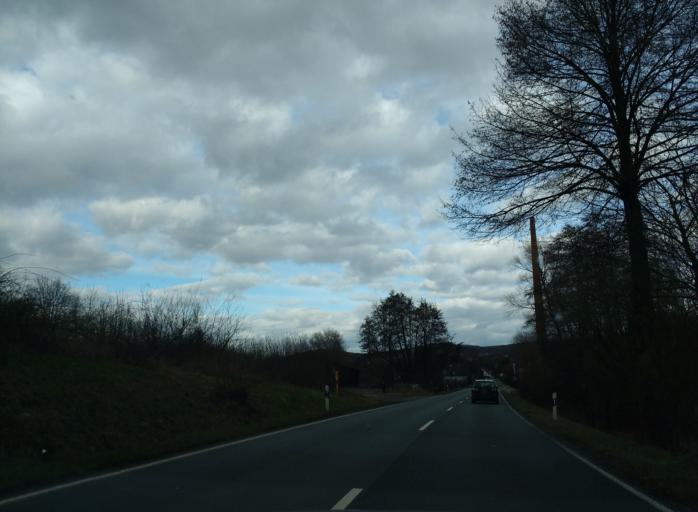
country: DE
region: North Rhine-Westphalia
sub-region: Regierungsbezirk Detmold
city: Lemgo
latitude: 52.1003
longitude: 8.9305
